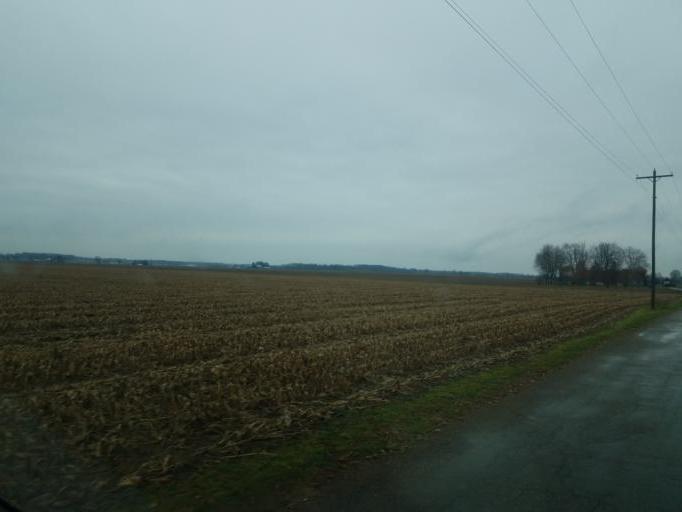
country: US
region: Ohio
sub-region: Knox County
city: Fredericktown
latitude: 40.4631
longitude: -82.5723
